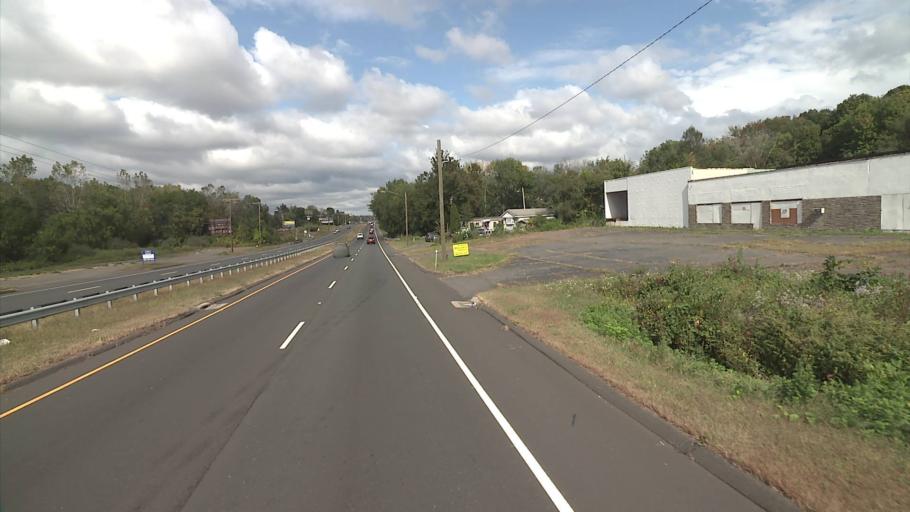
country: US
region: Connecticut
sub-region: Hartford County
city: Kensington
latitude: 41.6355
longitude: -72.7362
